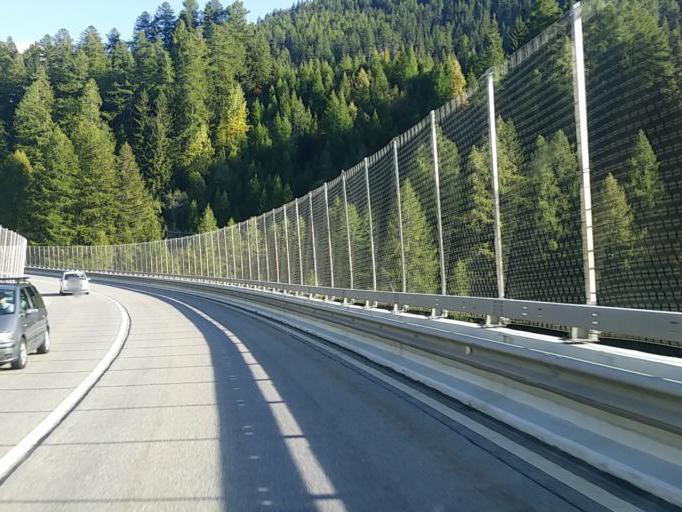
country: CH
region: Valais
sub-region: Brig District
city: Naters
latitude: 46.2953
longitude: 8.0522
